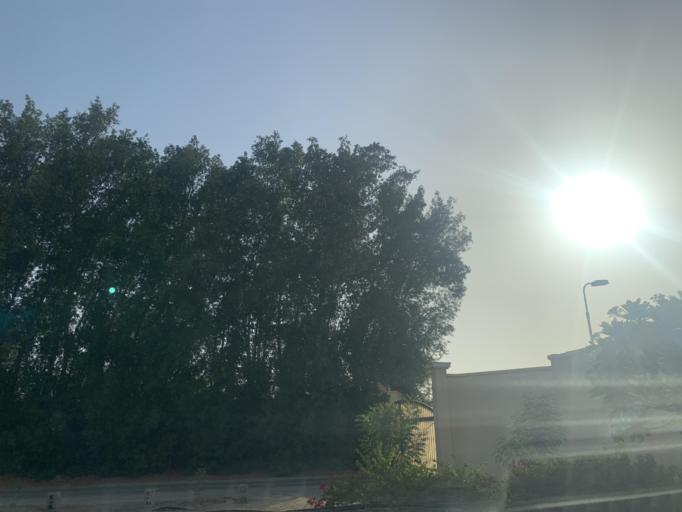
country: BH
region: Northern
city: Madinat `Isa
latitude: 26.1899
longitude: 50.4633
